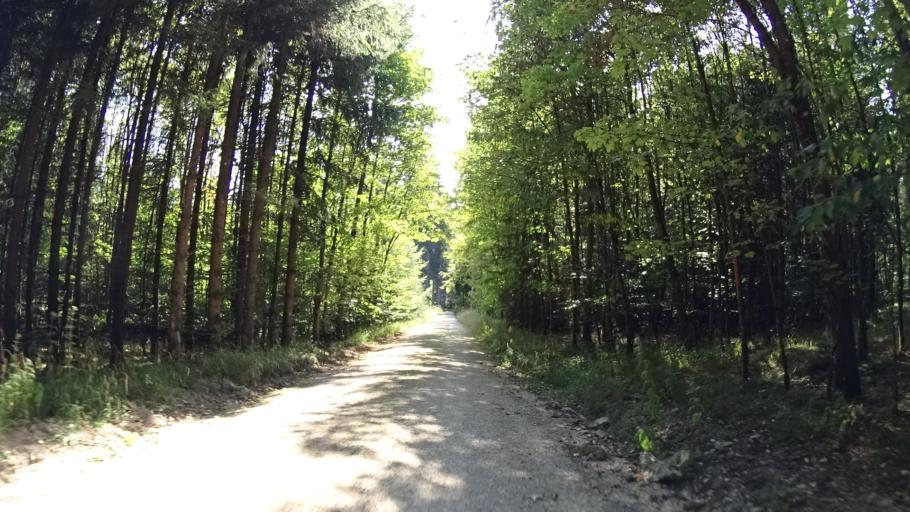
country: DE
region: Bavaria
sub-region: Upper Bavaria
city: Pollenfeld
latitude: 48.9498
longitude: 11.2540
